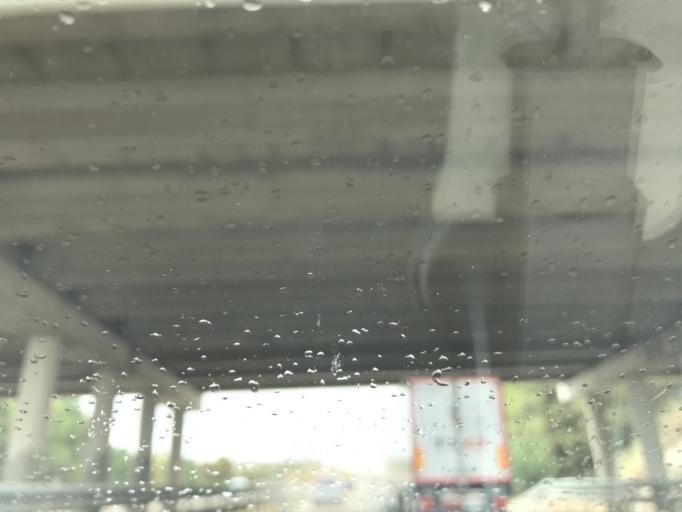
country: ES
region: Andalusia
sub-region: Provincia de Jaen
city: Bailen
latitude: 38.1209
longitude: -3.7606
